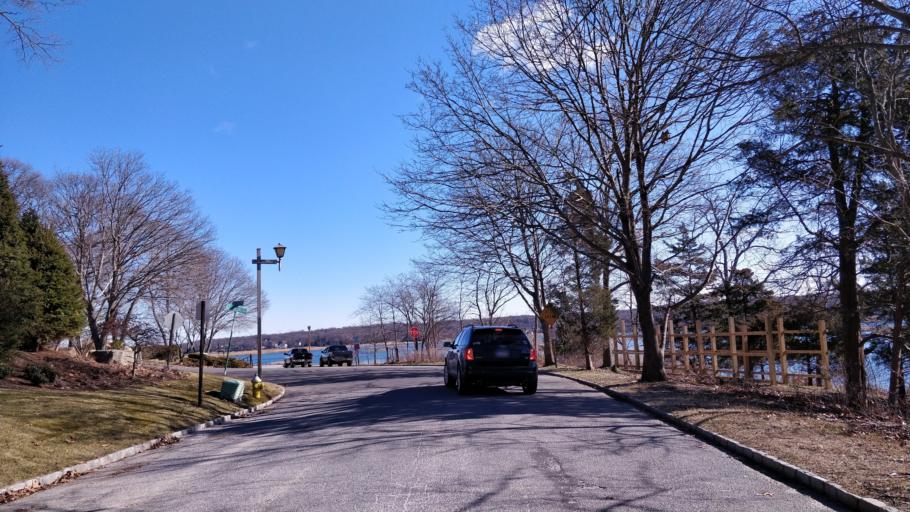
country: US
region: New York
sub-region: Suffolk County
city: Mount Sinai
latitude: 40.9576
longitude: -73.0422
